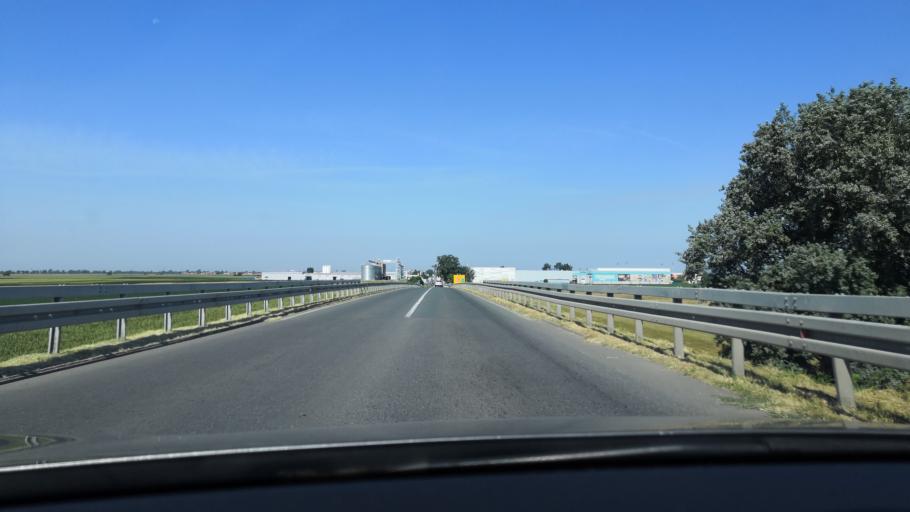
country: RS
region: Autonomna Pokrajina Vojvodina
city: Nova Pazova
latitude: 44.9864
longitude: 20.2147
